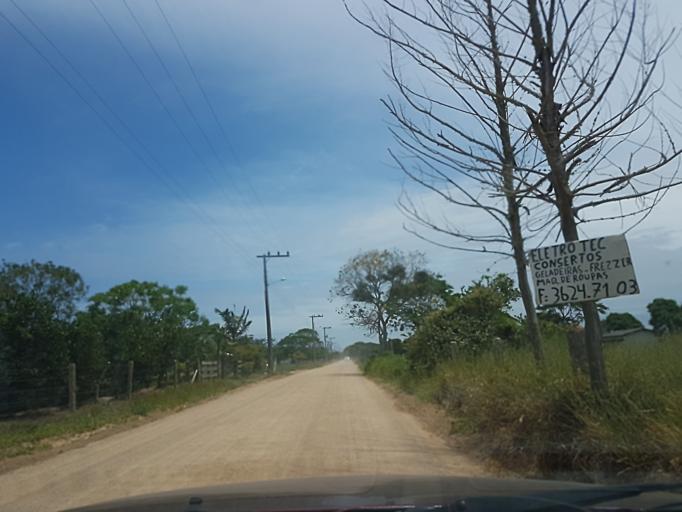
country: BR
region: Santa Catarina
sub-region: Jaguaruna
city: Jaguaruna
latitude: -28.6400
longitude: -48.9624
